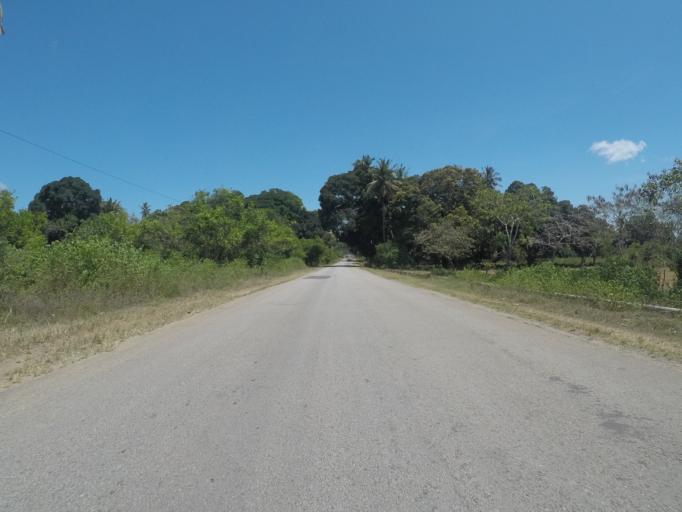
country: TZ
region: Zanzibar Central/South
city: Nganane
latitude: -6.2921
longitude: 39.4389
